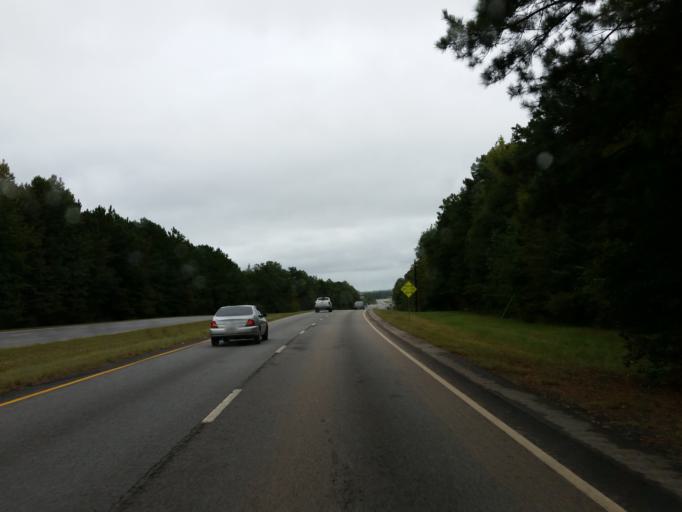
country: US
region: Georgia
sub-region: Clayton County
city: Lovejoy
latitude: 33.4109
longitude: -84.3137
